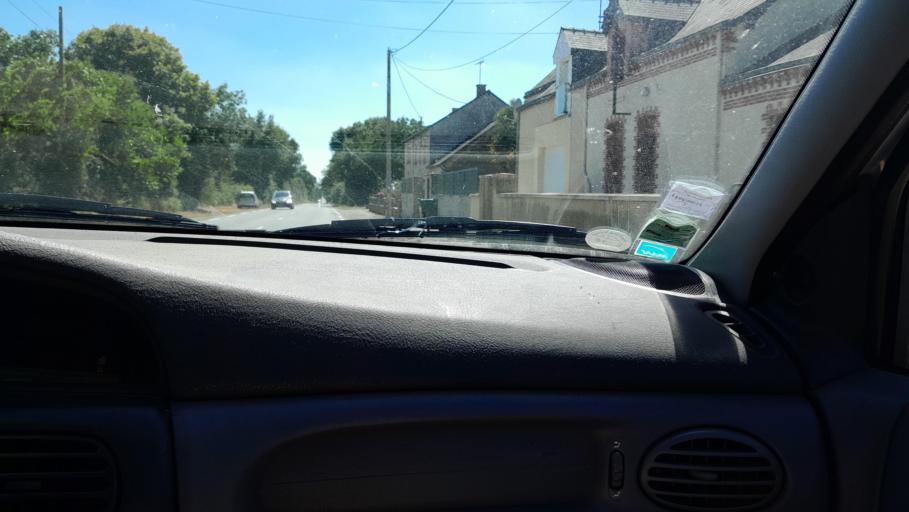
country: FR
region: Pays de la Loire
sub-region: Departement de Maine-et-Loire
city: Pouance
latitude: 47.6674
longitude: -1.1911
